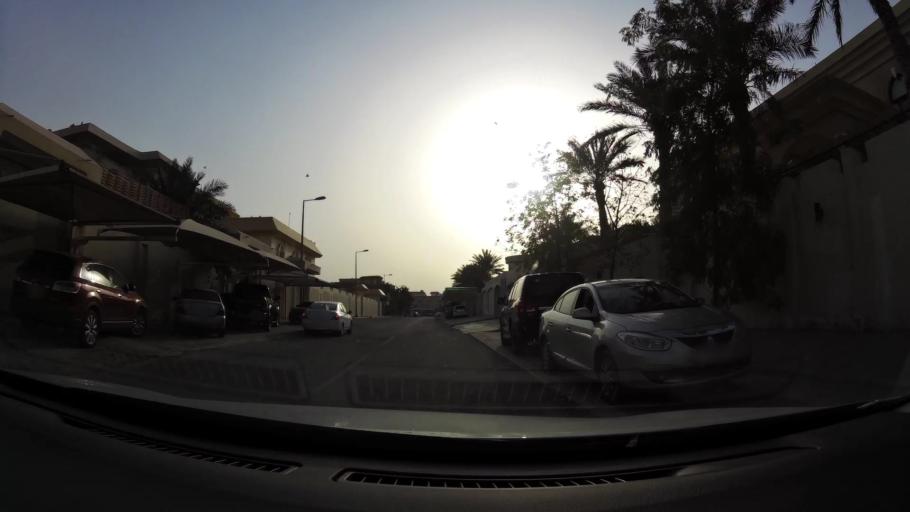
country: QA
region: Baladiyat ar Rayyan
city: Ar Rayyan
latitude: 25.2502
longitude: 51.4471
